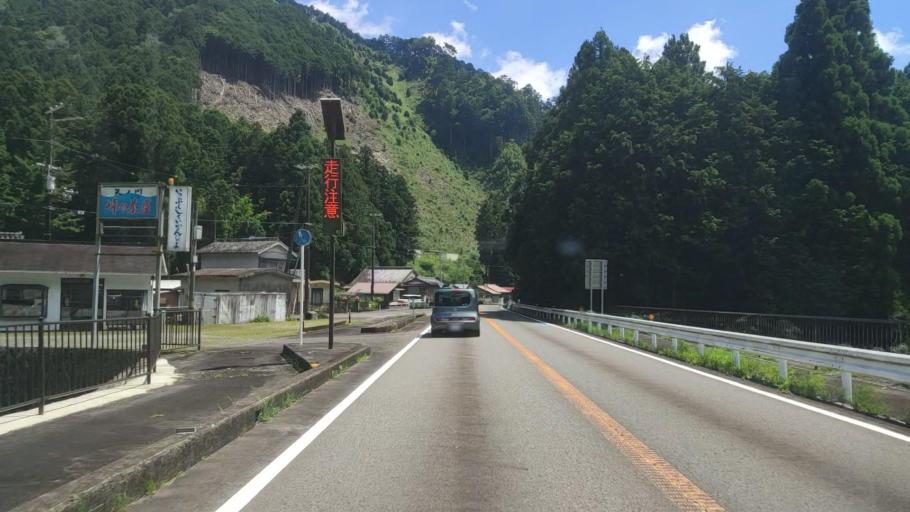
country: JP
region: Mie
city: Owase
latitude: 33.9847
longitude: 136.1082
